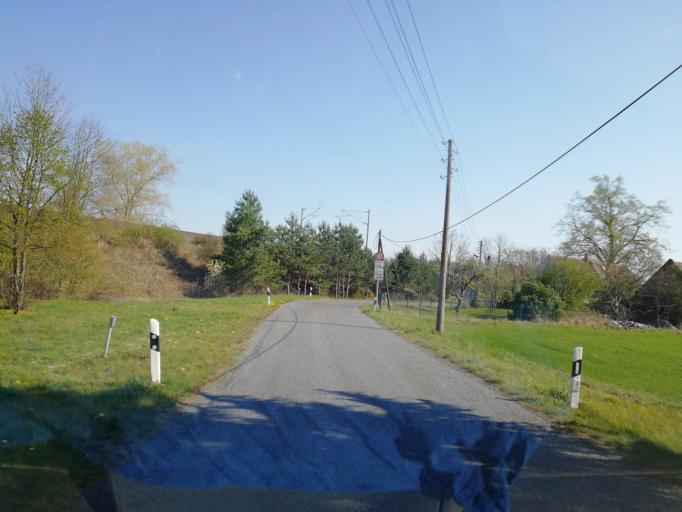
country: DE
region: Brandenburg
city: Bronkow
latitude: 51.6985
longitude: 13.8737
